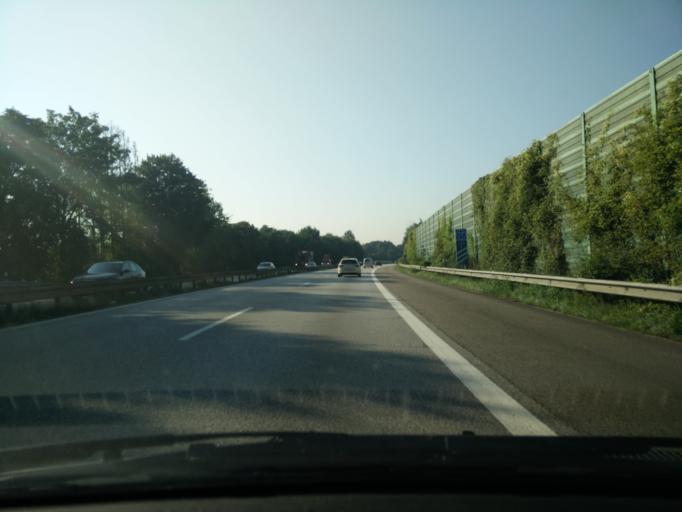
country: DE
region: Schleswig-Holstein
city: Rellingen
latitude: 53.6596
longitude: 9.8200
